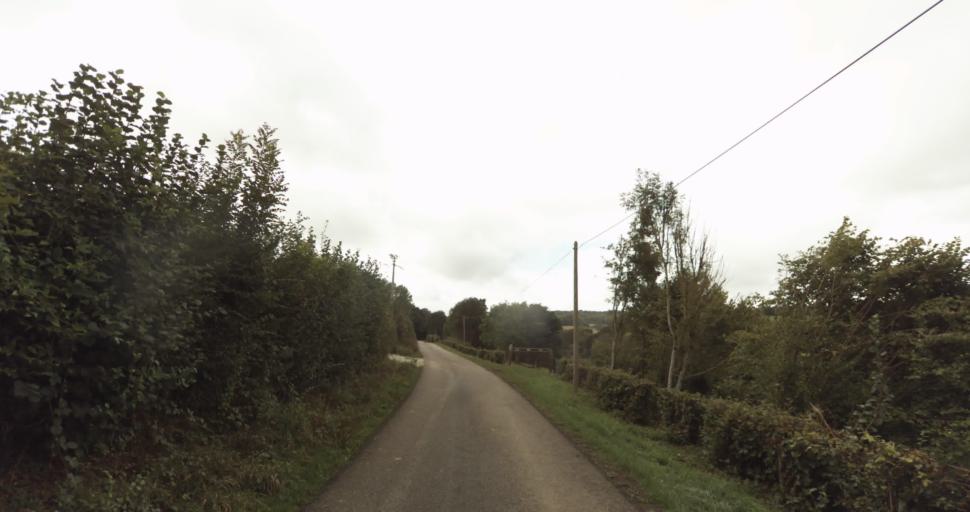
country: FR
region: Lower Normandy
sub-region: Departement de l'Orne
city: Gace
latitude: 48.8084
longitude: 0.2826
